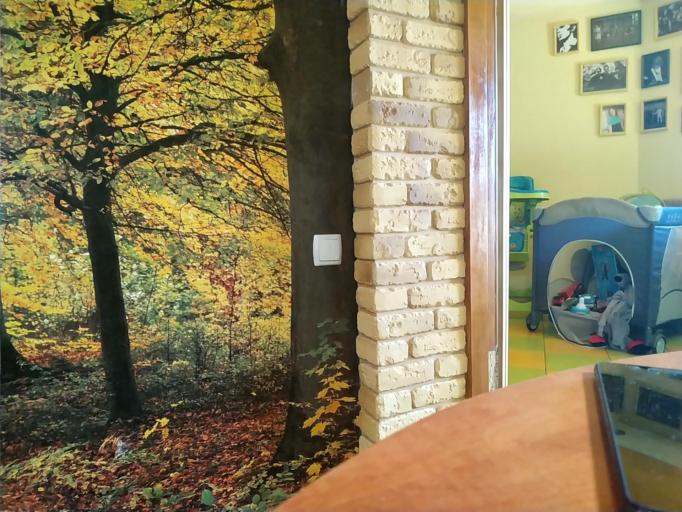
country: RU
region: Tverskaya
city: Velikooktyabr'skiy
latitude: 57.5188
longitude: 34.0681
